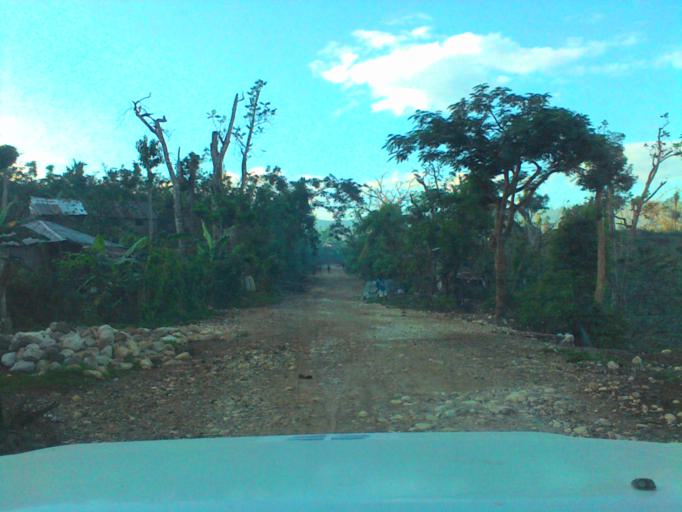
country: HT
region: Grandans
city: Jeremie
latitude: 18.5481
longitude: -74.1093
